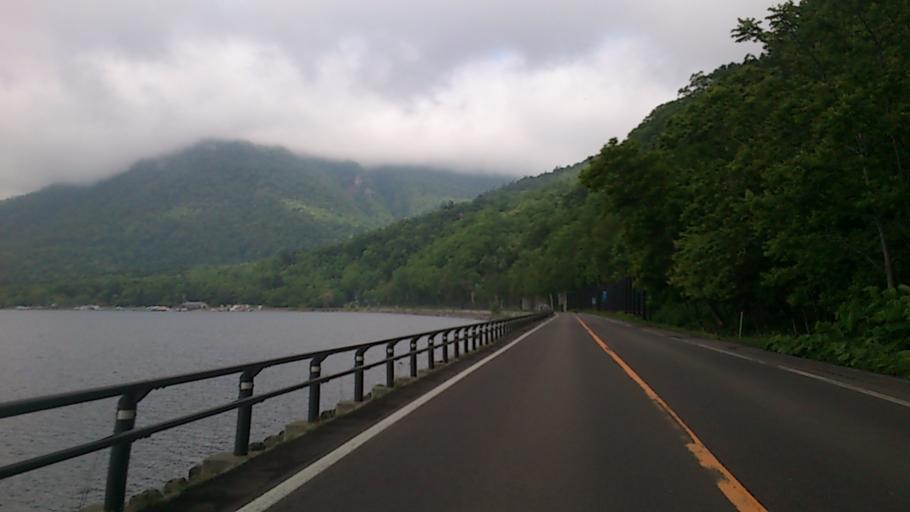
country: JP
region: Hokkaido
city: Shiraoi
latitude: 42.8043
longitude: 141.3372
